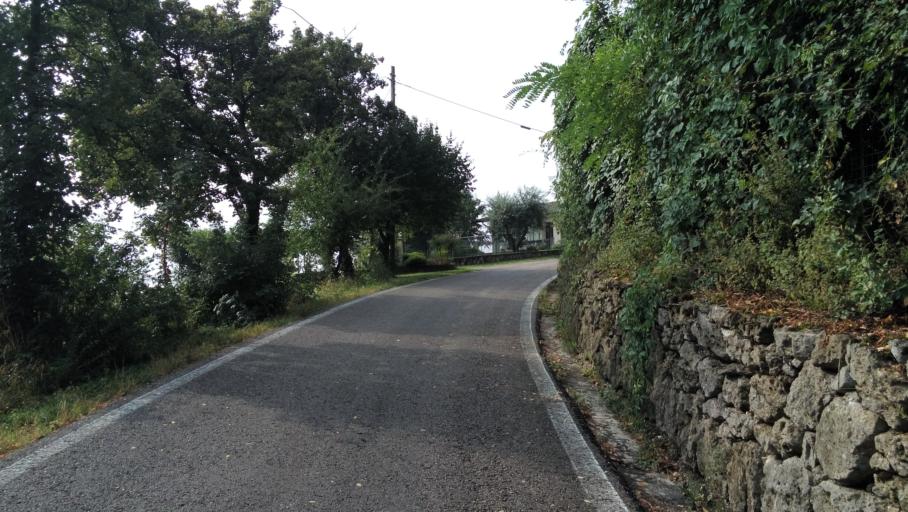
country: IT
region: Veneto
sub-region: Provincia di Vicenza
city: Monteviale
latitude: 45.5489
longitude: 11.4620
